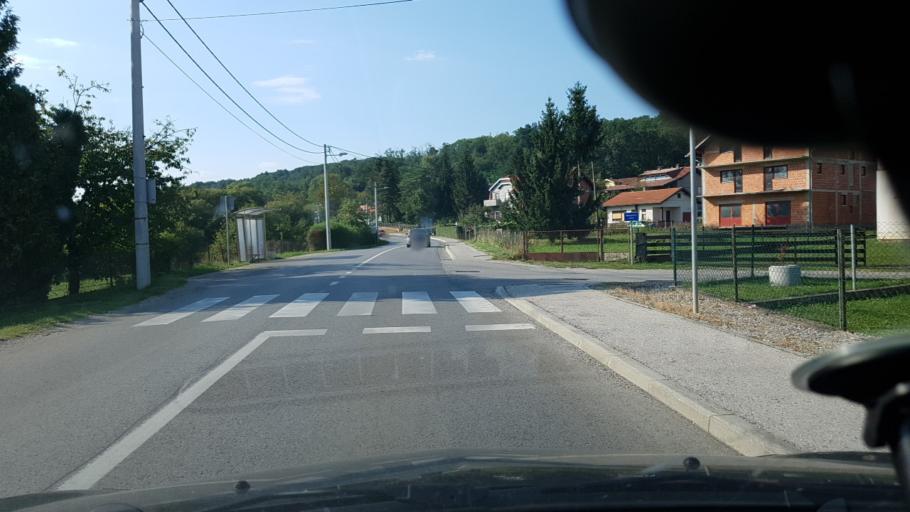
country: HR
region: Zagrebacka
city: Brdovec
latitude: 45.8722
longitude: 15.7520
